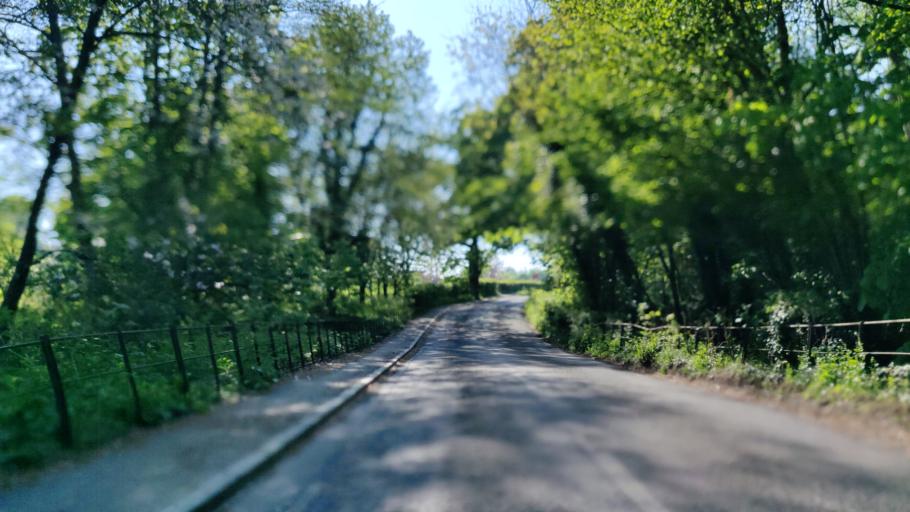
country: GB
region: England
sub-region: West Sussex
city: Southwater
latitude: 51.0465
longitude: -0.3547
